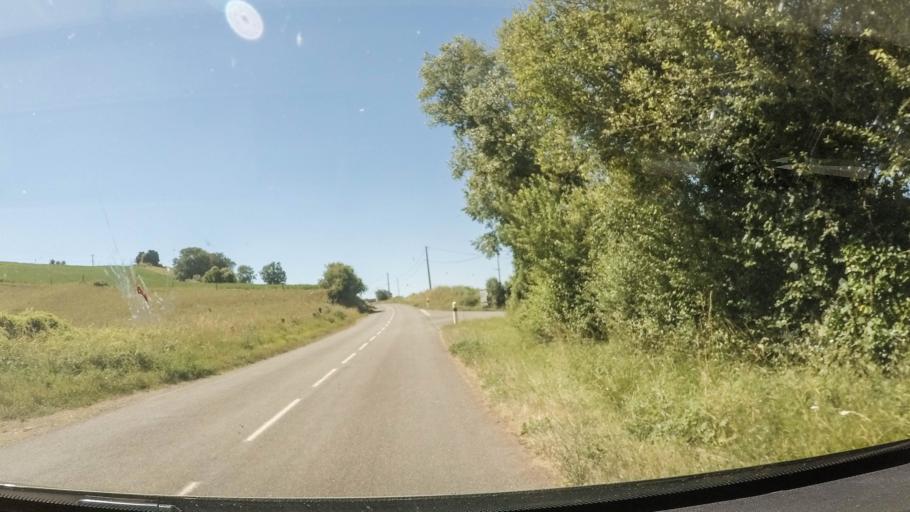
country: FR
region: Midi-Pyrenees
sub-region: Departement de l'Aveyron
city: Saint-Christophe-Vallon
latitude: 44.4698
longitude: 2.3679
